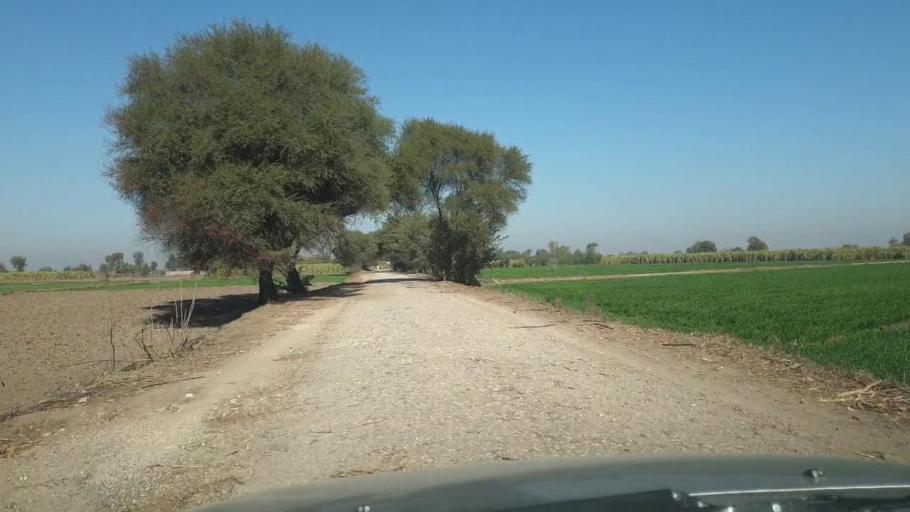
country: PK
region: Sindh
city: Ghotki
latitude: 28.0916
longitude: 69.3434
